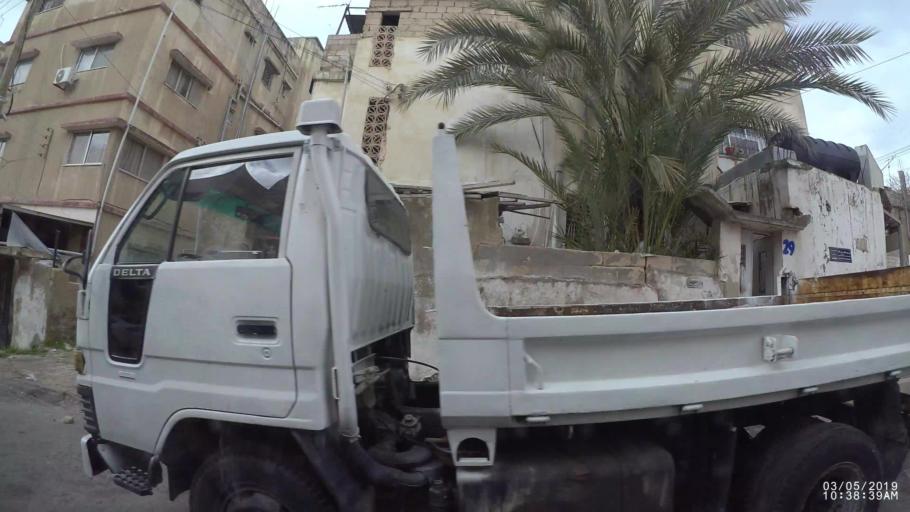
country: JO
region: Amman
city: Amman
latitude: 31.9814
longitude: 35.9235
